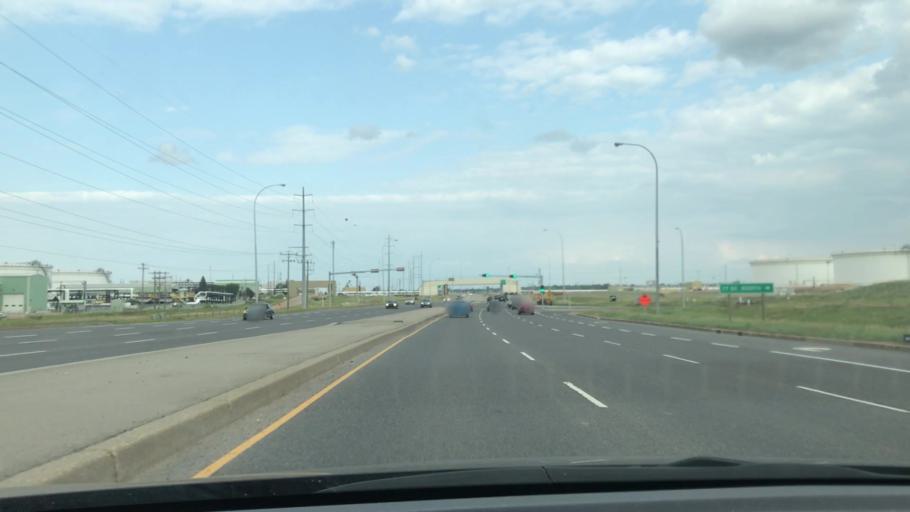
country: CA
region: Alberta
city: Sherwood Park
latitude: 53.5410
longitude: -113.3685
